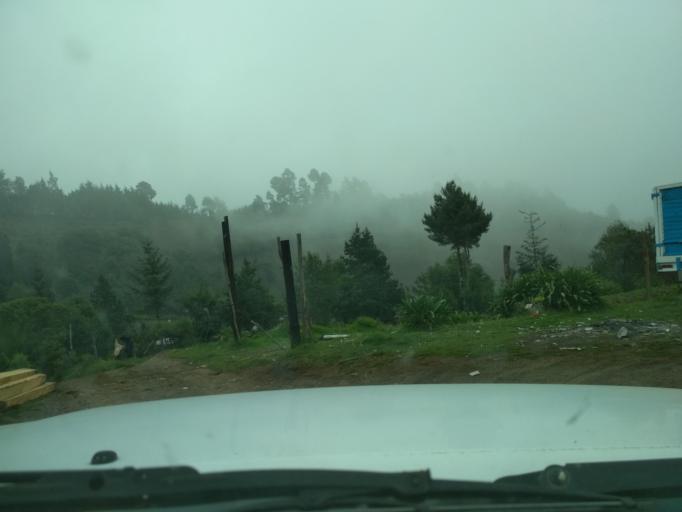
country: MX
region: Veracruz
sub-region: La Perla
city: Chilapa
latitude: 18.9769
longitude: -97.2013
